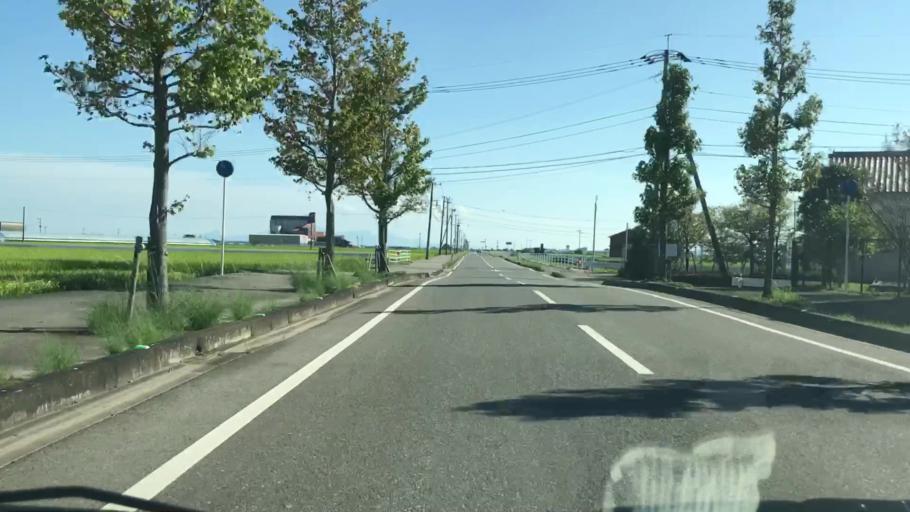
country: JP
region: Saga Prefecture
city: Okawa
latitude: 33.1792
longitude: 130.3128
